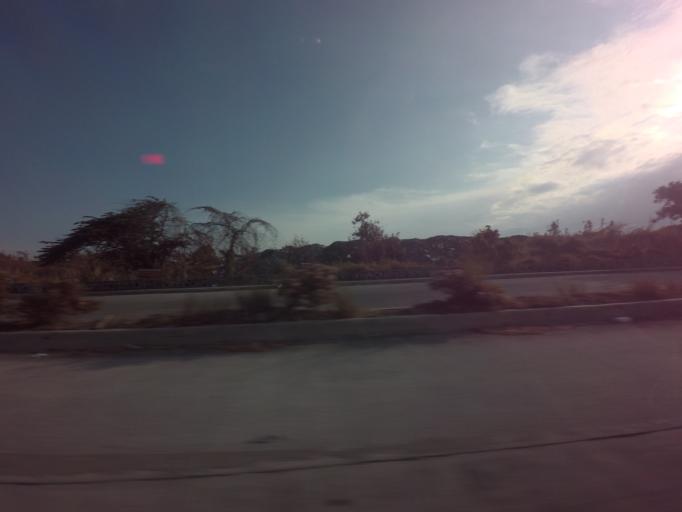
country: PH
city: Sambayanihan People's Village
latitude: 14.5021
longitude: 121.0139
